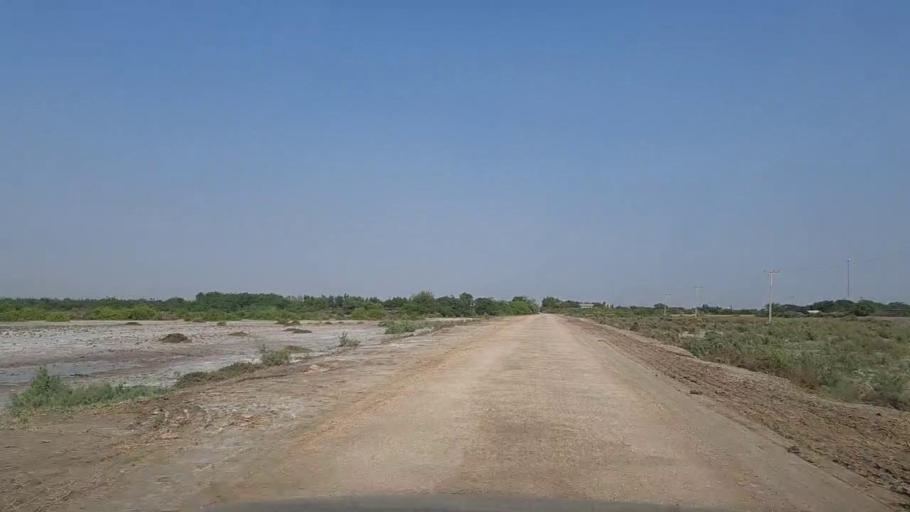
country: PK
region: Sindh
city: Thatta
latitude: 24.6102
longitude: 67.9565
